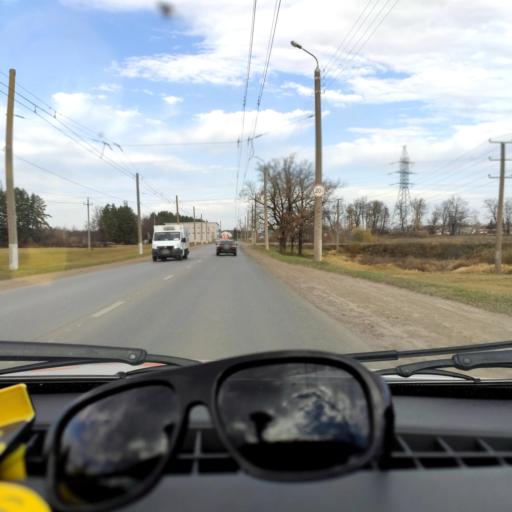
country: RU
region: Bashkortostan
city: Ufa
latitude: 54.7797
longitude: 55.9484
